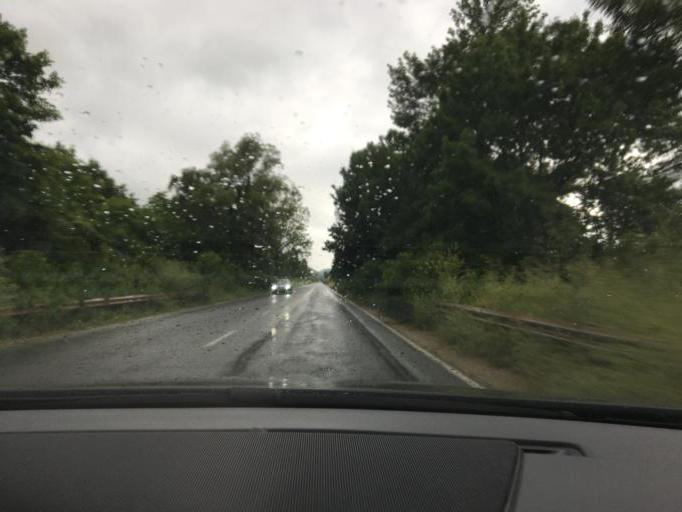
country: BG
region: Kyustendil
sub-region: Obshtina Kyustendil
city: Kyustendil
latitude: 42.2666
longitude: 22.6106
